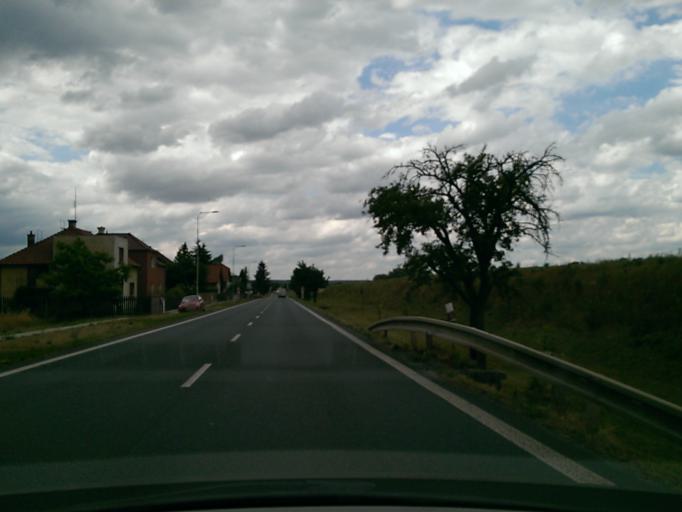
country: CZ
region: Central Bohemia
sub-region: Okres Nymburk
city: Nymburk
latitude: 50.2223
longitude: 15.0281
